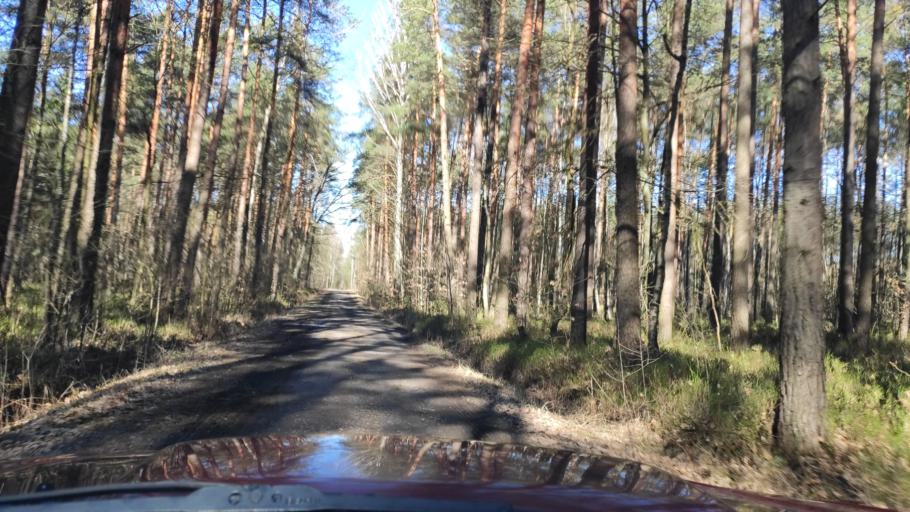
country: PL
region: Masovian Voivodeship
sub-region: Powiat kozienicki
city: Garbatka-Letnisko
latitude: 51.4393
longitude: 21.5431
